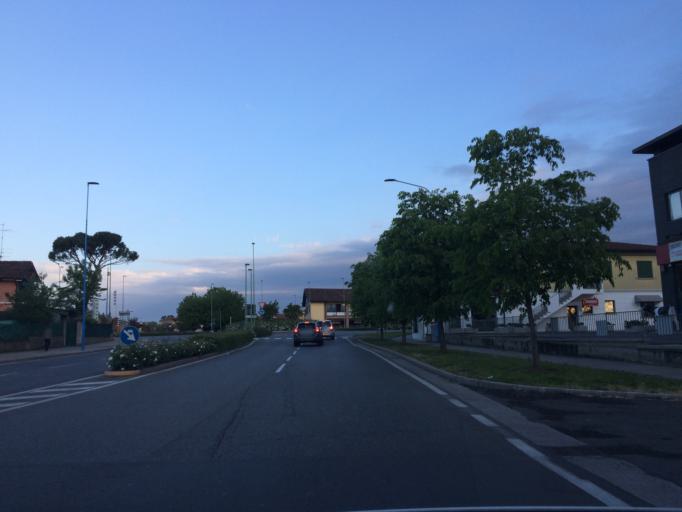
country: IT
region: Lombardy
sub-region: Provincia di Brescia
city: San Zeno Naviglio
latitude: 45.5136
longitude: 10.2279
